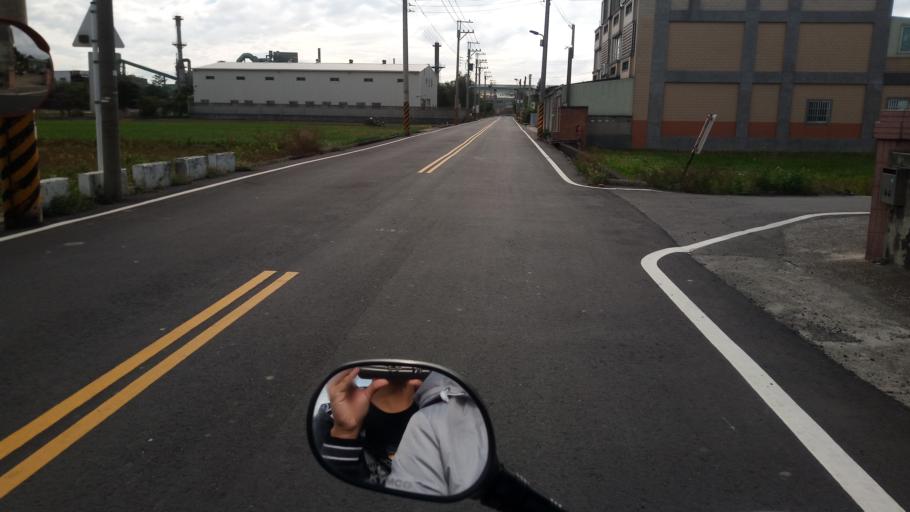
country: TW
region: Taiwan
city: Fengyuan
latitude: 24.4140
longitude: 120.6492
